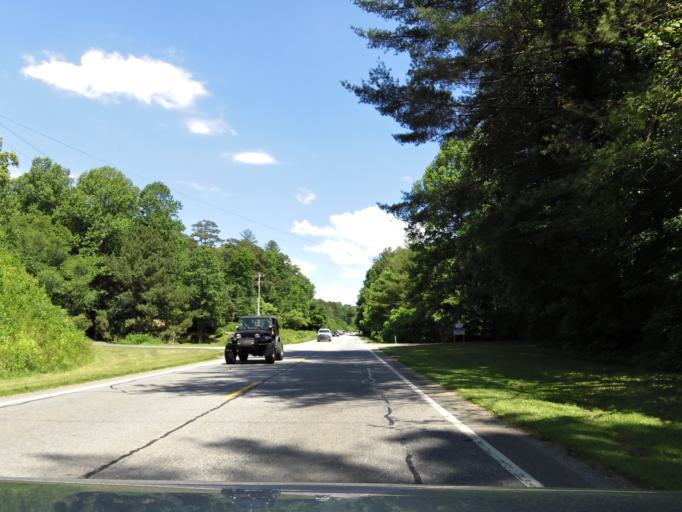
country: US
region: Georgia
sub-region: Union County
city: Blairsville
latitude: 34.8962
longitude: -84.0004
